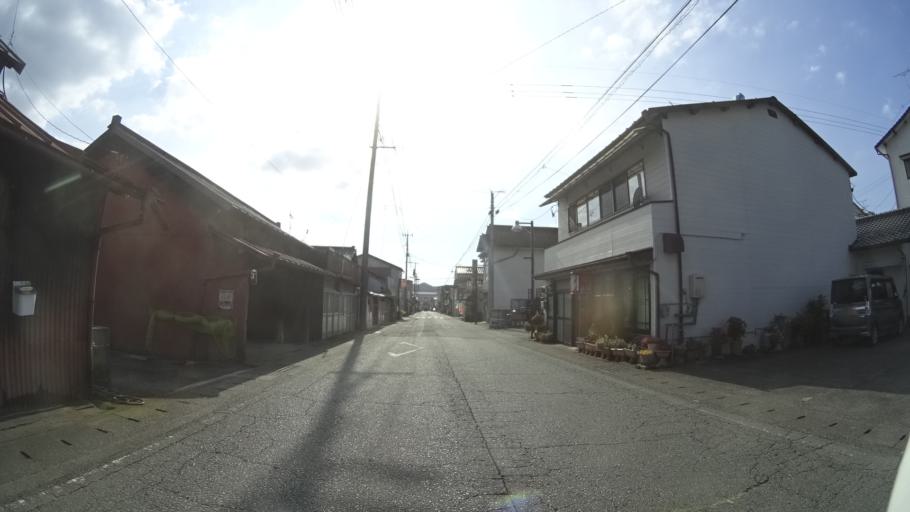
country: JP
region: Kumamoto
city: Ozu
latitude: 32.6862
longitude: 130.9950
